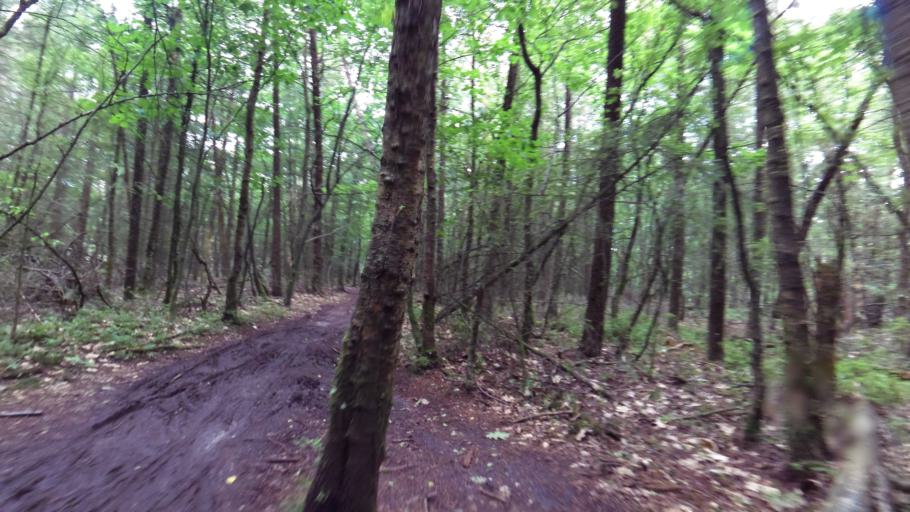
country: NL
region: Gelderland
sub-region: Gemeente Apeldoorn
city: Apeldoorn
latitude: 52.2114
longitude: 5.8971
